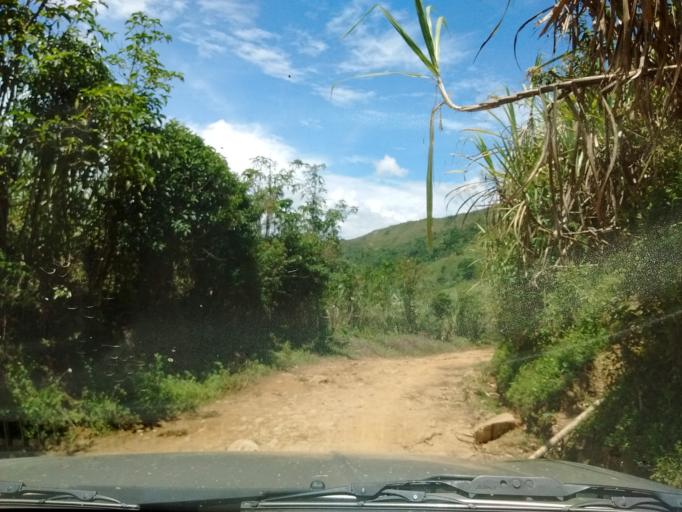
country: CO
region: Cauca
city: Villa Rica
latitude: 2.6295
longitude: -76.7717
